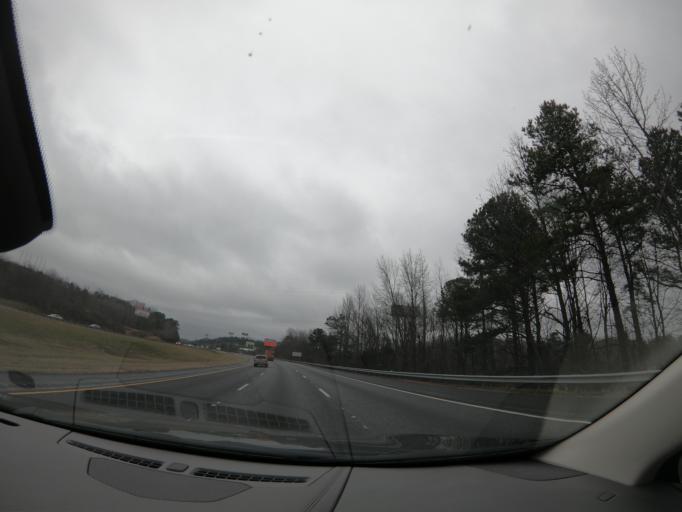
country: US
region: Georgia
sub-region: Whitfield County
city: Varnell
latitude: 34.8562
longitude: -85.0188
